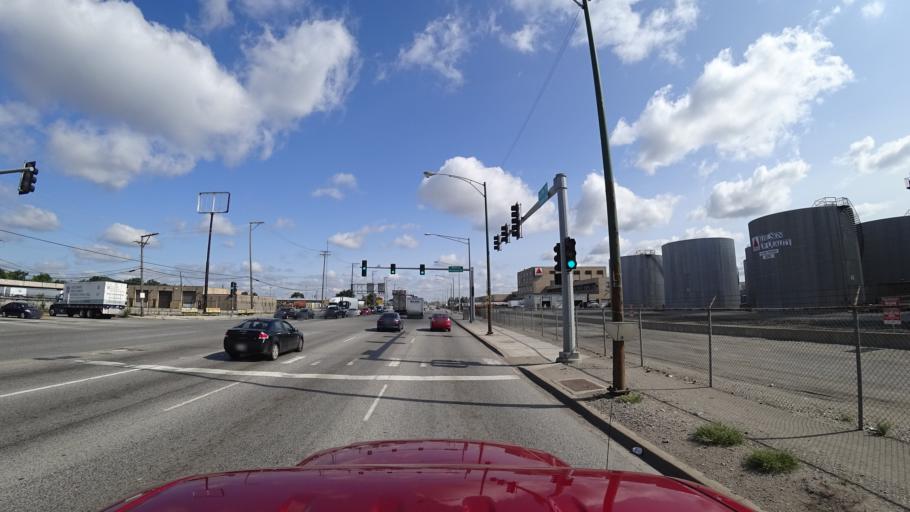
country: US
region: Illinois
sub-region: Cook County
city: Cicero
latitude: 41.8217
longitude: -87.7434
